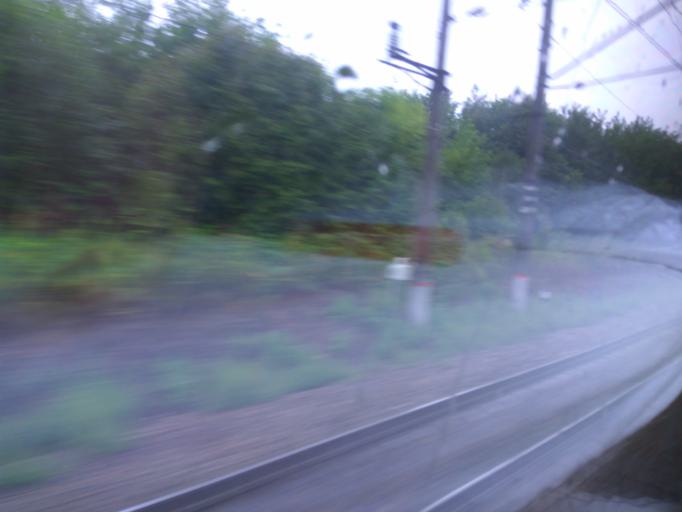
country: RU
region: Moskovskaya
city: Kashira
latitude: 54.8579
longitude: 38.2064
